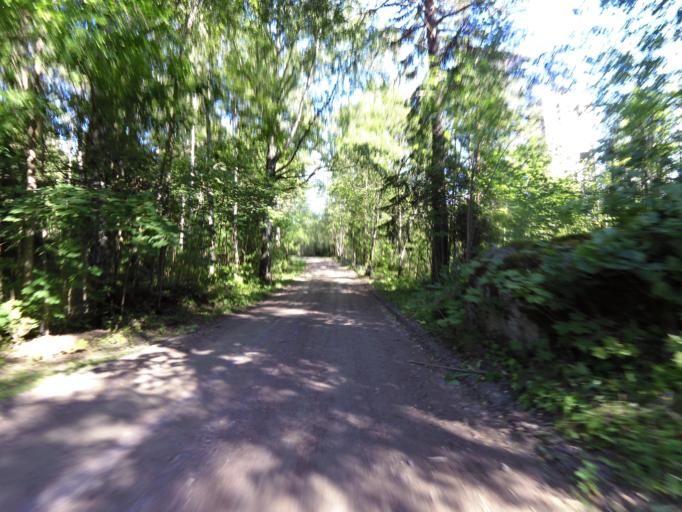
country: SE
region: Gaevleborg
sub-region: Hofors Kommun
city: Hofors
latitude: 60.5303
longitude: 16.4078
